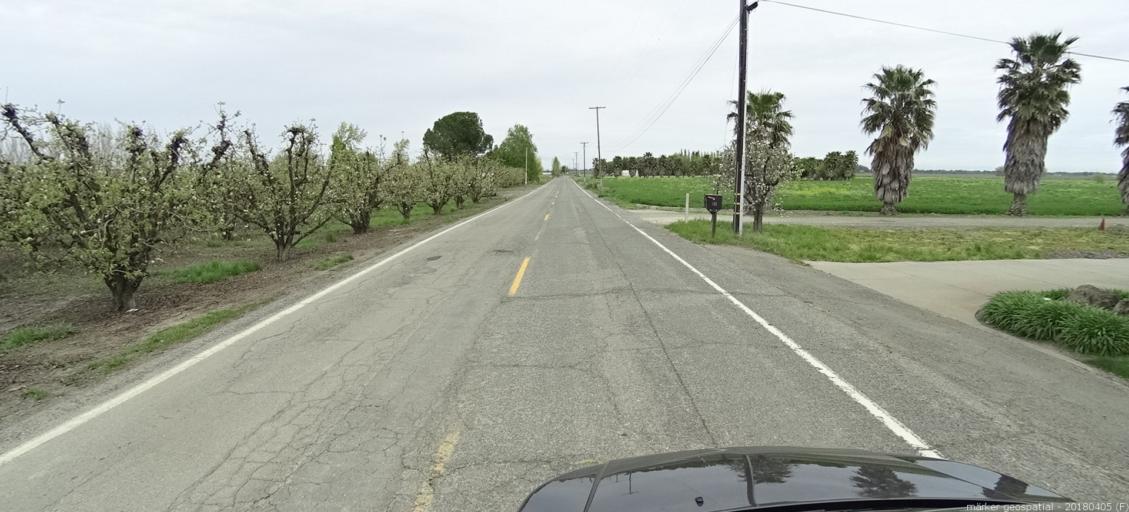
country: US
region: California
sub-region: Sacramento County
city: Walnut Grove
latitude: 38.2788
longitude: -121.5394
